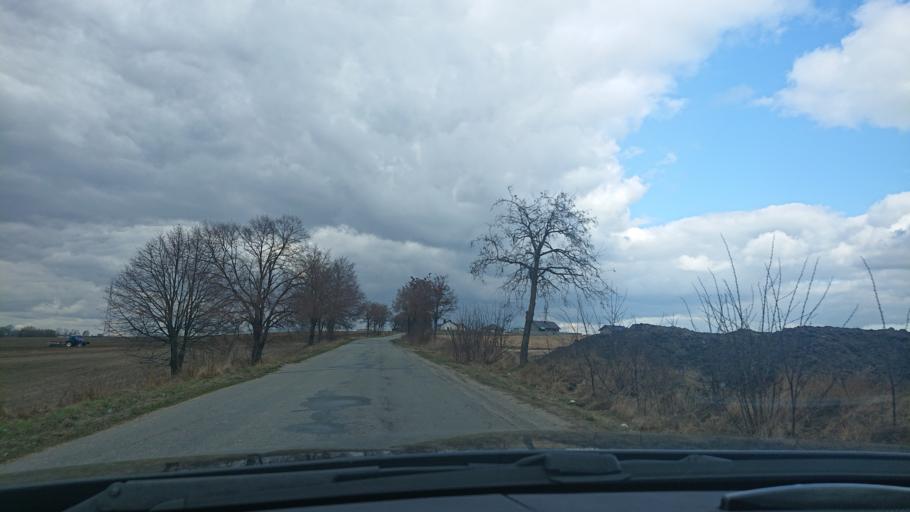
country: PL
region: Greater Poland Voivodeship
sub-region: Powiat gnieznienski
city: Niechanowo
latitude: 52.5579
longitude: 17.6972
